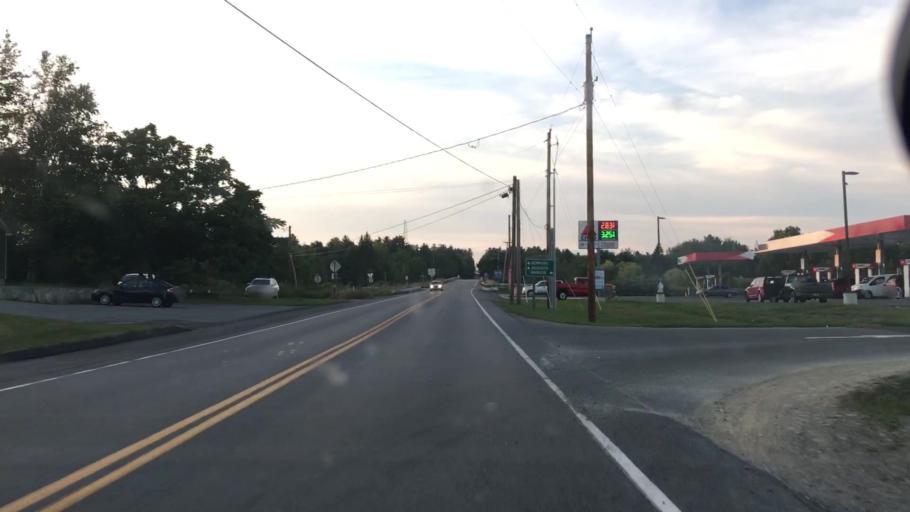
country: US
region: Maine
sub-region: Penobscot County
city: Hermon
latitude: 44.7560
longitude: -68.9732
